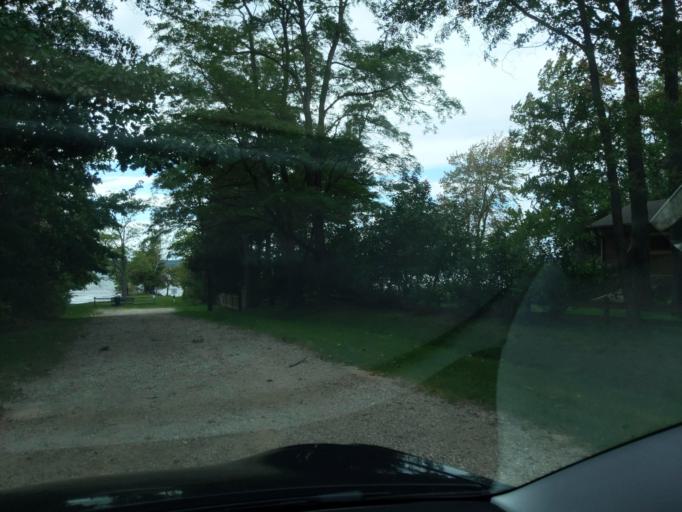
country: US
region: Michigan
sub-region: Kalkaska County
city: Rapid City
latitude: 44.8848
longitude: -85.2742
